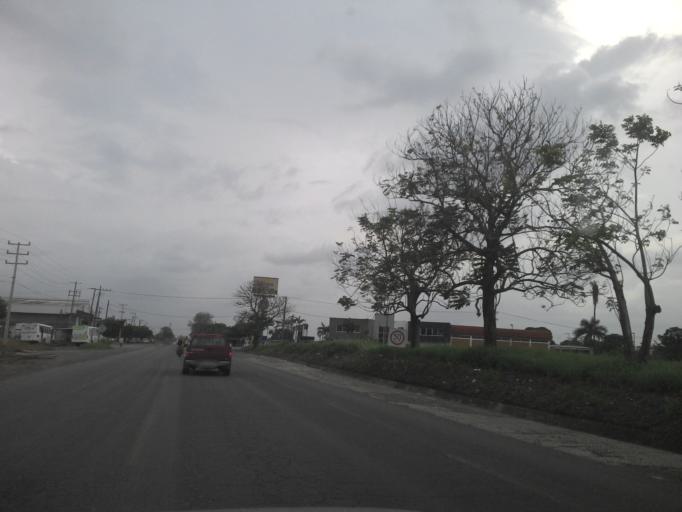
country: MX
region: Veracruz
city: Martinez de la Torre
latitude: 20.0798
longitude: -97.0454
